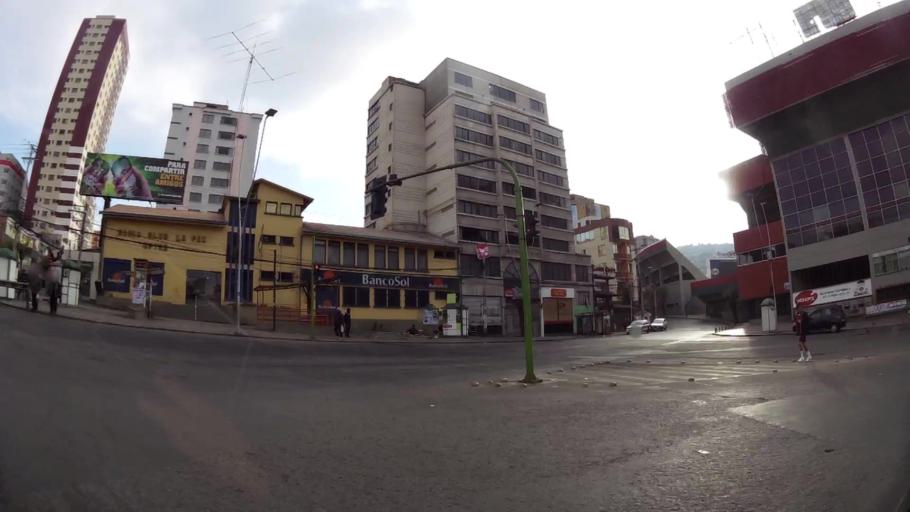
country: BO
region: La Paz
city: La Paz
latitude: -16.4993
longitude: -68.1241
